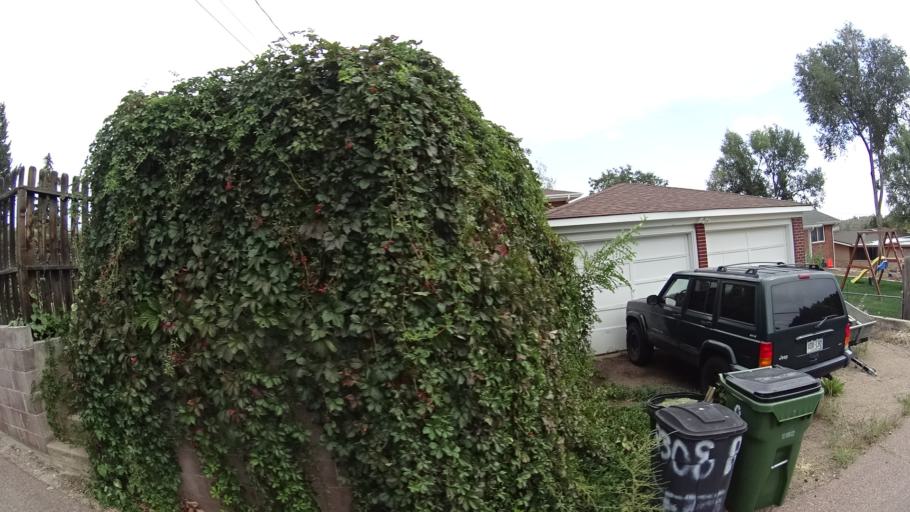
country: US
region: Colorado
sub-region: El Paso County
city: Colorado Springs
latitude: 38.8603
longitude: -104.7868
